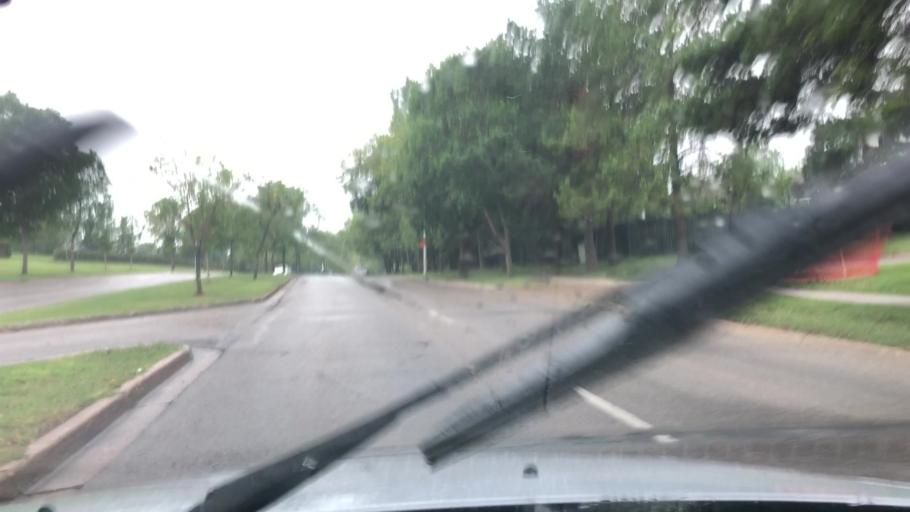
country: CA
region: Alberta
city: St. Albert
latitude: 53.6423
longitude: -113.6303
